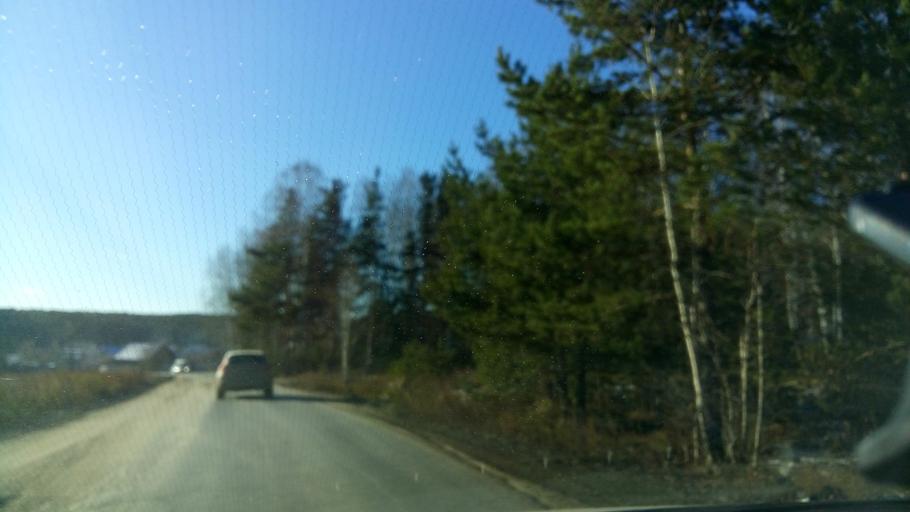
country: RU
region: Sverdlovsk
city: Gornyy Shchit
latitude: 56.7175
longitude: 60.5170
